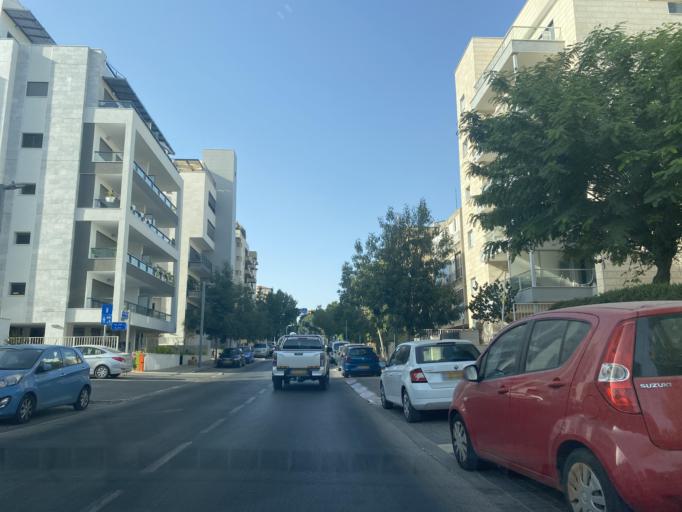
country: IL
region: Tel Aviv
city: Ramat HaSharon
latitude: 32.1655
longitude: 34.8486
